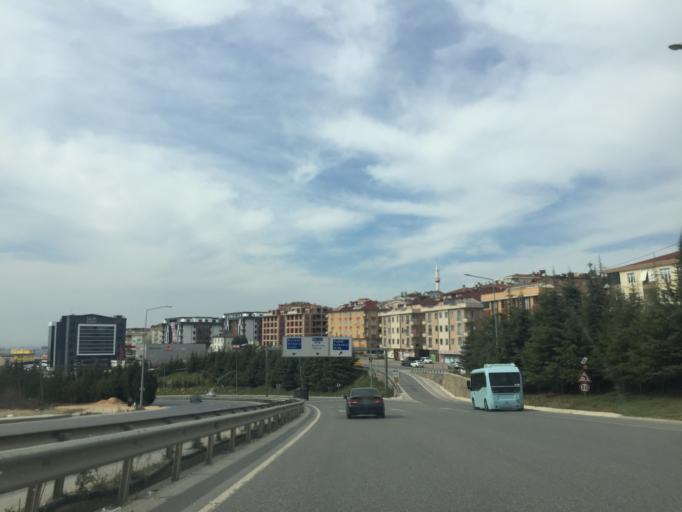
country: TR
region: Kocaeli
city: Gebze
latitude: 40.7905
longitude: 29.4141
